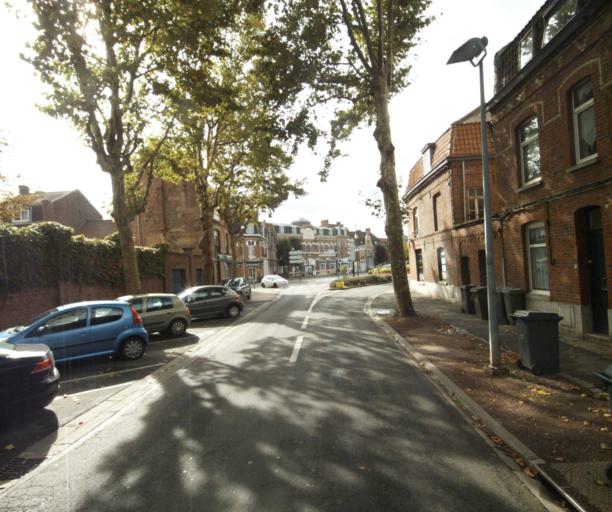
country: FR
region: Nord-Pas-de-Calais
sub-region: Departement du Nord
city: Armentieres
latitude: 50.6828
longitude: 2.8868
